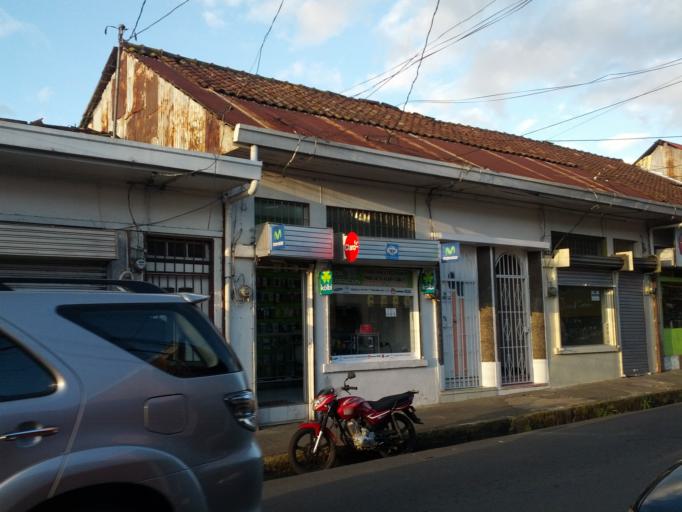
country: CR
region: Alajuela
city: Alajuela
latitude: 10.0139
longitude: -84.2149
